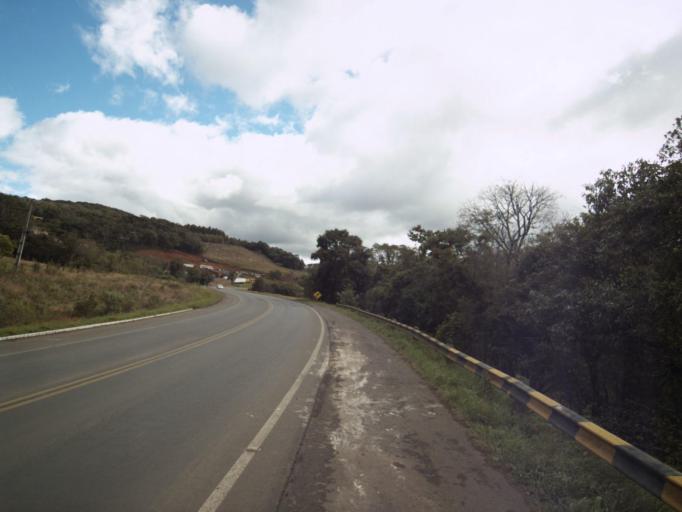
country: BR
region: Santa Catarina
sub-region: Concordia
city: Concordia
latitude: -27.2325
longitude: -51.9501
